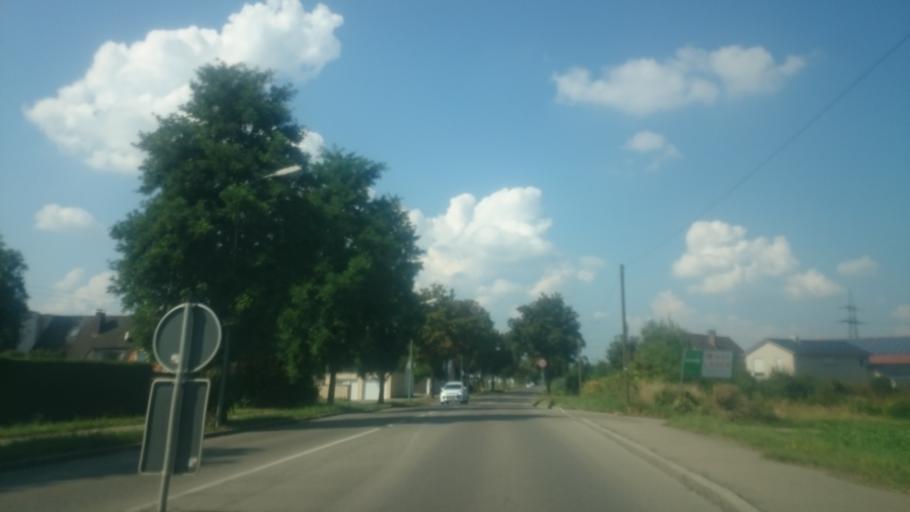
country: DE
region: Bavaria
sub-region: Swabia
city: Friedberg
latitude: 48.3659
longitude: 10.9479
